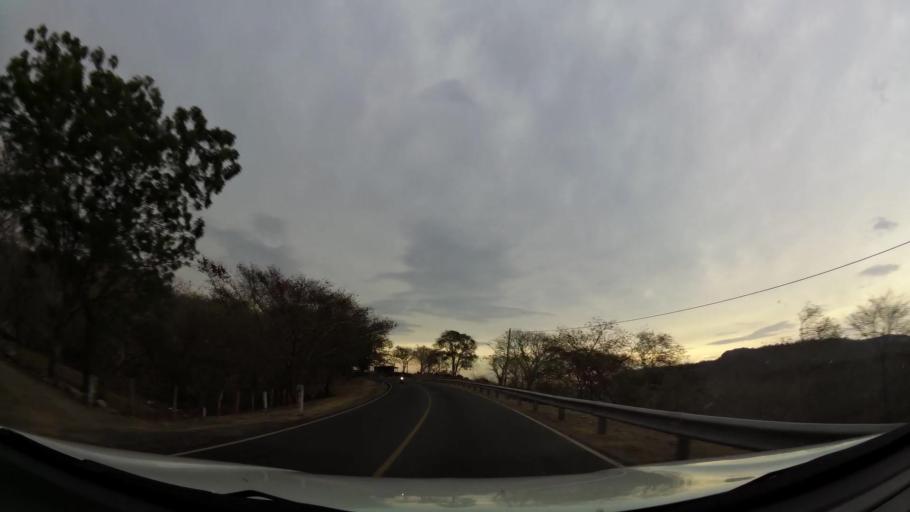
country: NI
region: Leon
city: La Jicaral
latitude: 12.6746
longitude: -86.4276
